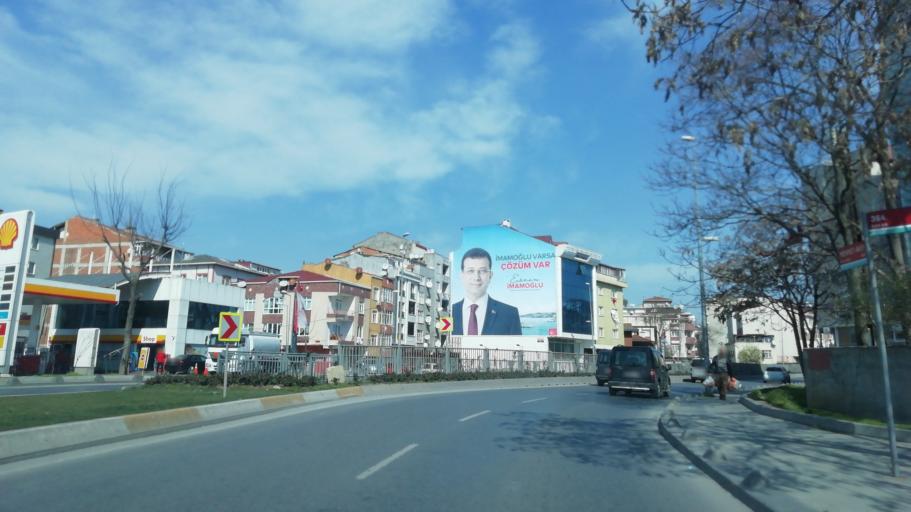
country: TR
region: Istanbul
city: Bagcilar
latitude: 41.0284
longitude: 28.8469
